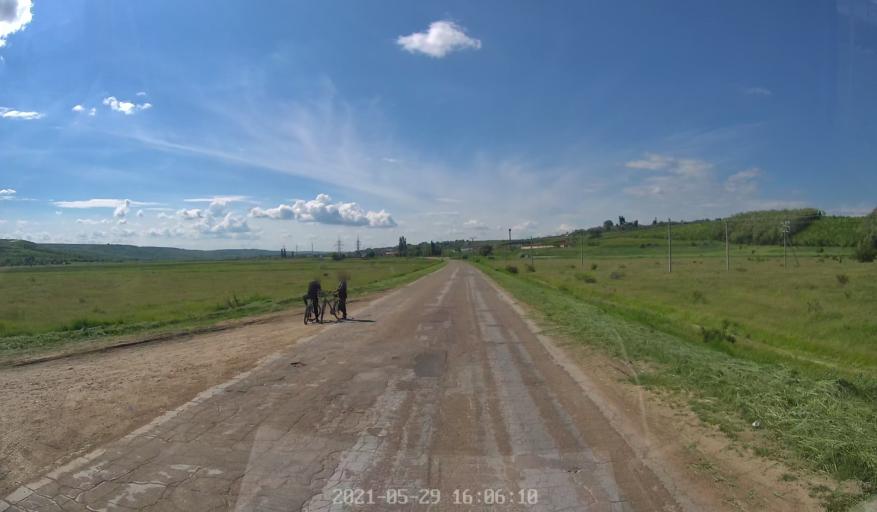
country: MD
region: Chisinau
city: Singera
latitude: 46.8135
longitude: 28.9089
